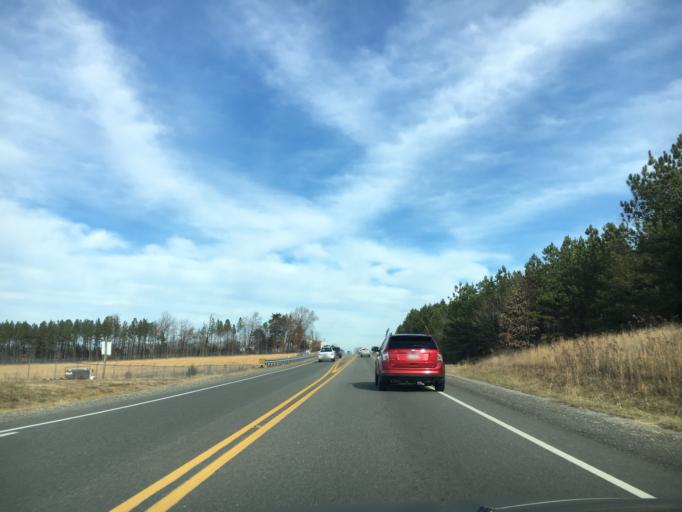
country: US
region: Virginia
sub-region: Louisa County
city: Louisa
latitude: 38.0762
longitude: -77.8813
